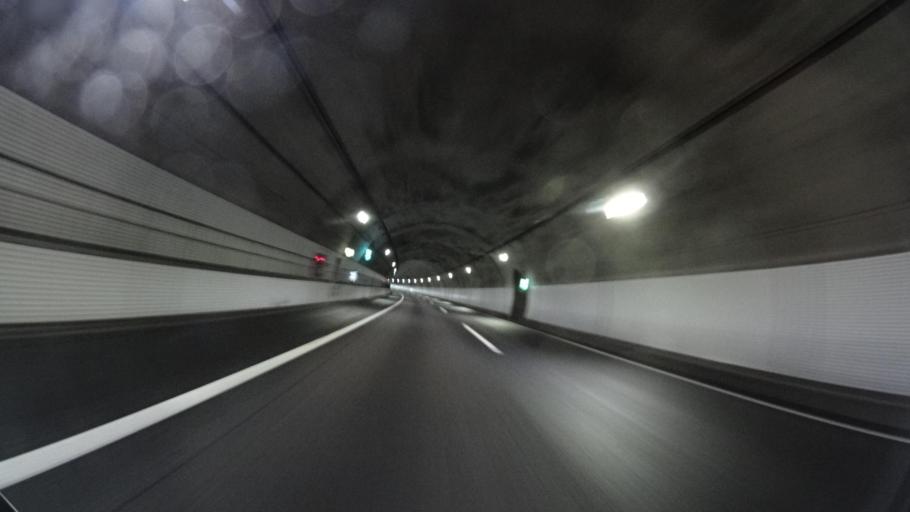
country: JP
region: Mie
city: Kameyama
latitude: 34.9168
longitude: 136.4205
